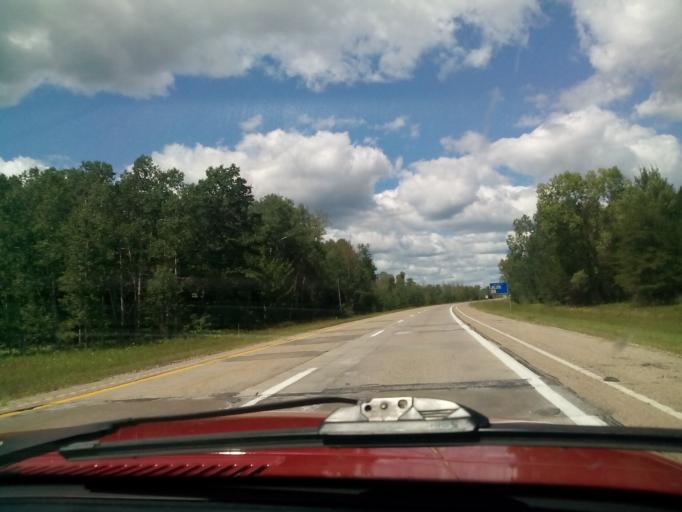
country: US
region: Michigan
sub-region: Ogemaw County
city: West Branch
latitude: 44.2204
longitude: -84.2066
